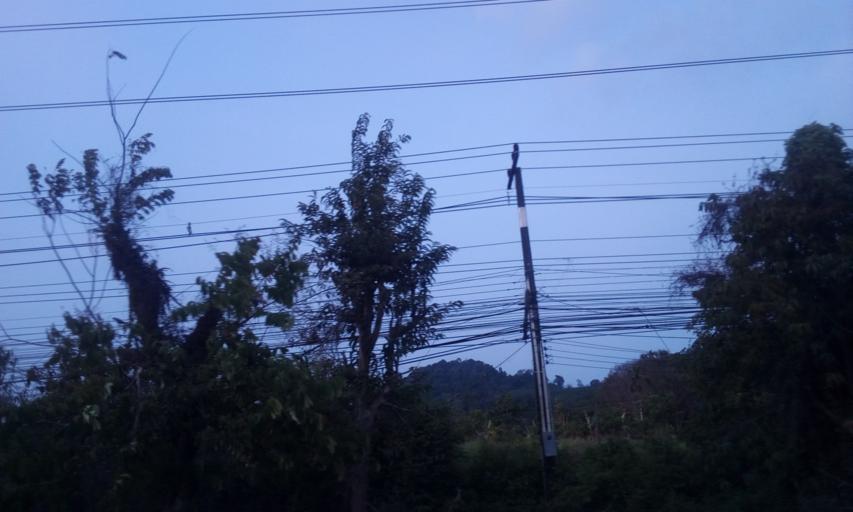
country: TH
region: Trat
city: Khao Saming
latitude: 12.3692
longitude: 102.3916
